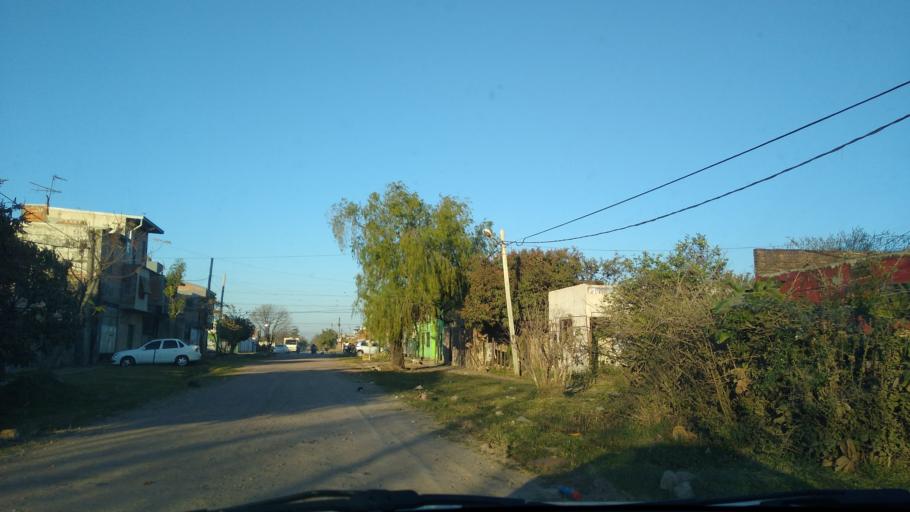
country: AR
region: Chaco
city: Resistencia
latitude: -27.4783
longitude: -58.9688
